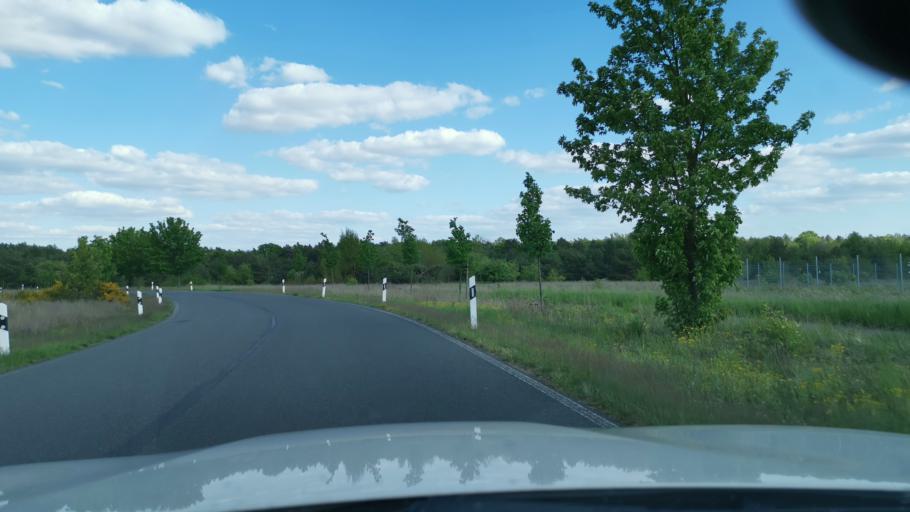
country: DE
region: Brandenburg
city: Niedergorsdorf
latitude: 51.9932
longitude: 13.0013
